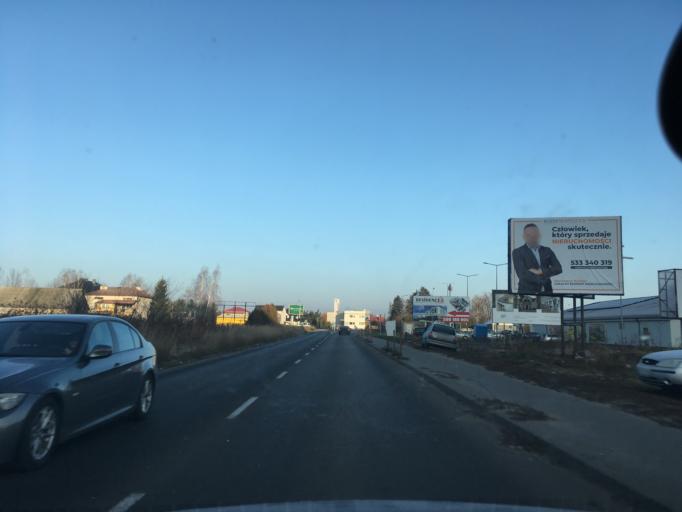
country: PL
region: Masovian Voivodeship
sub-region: Powiat piaseczynski
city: Piaseczno
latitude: 52.0808
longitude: 21.0083
